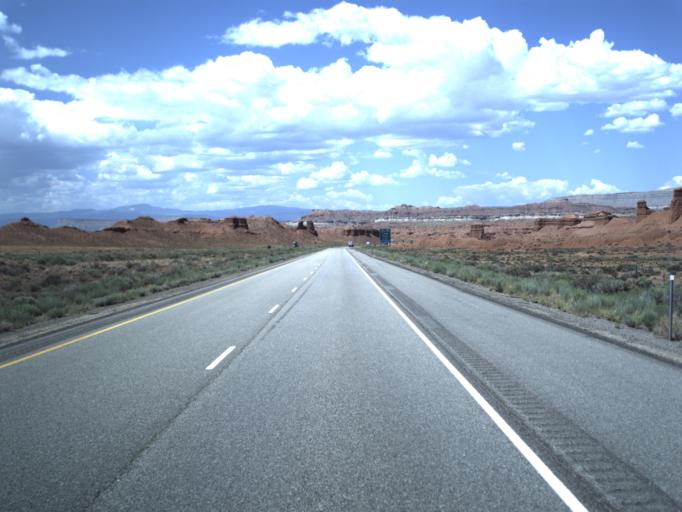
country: US
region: Utah
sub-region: Emery County
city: Ferron
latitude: 38.8467
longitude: -111.0387
